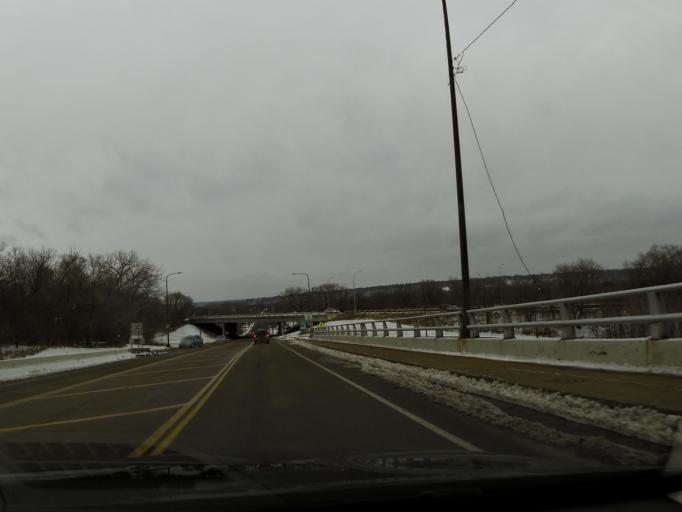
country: US
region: Minnesota
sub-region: Dakota County
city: West Saint Paul
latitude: 44.9306
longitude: -93.1443
